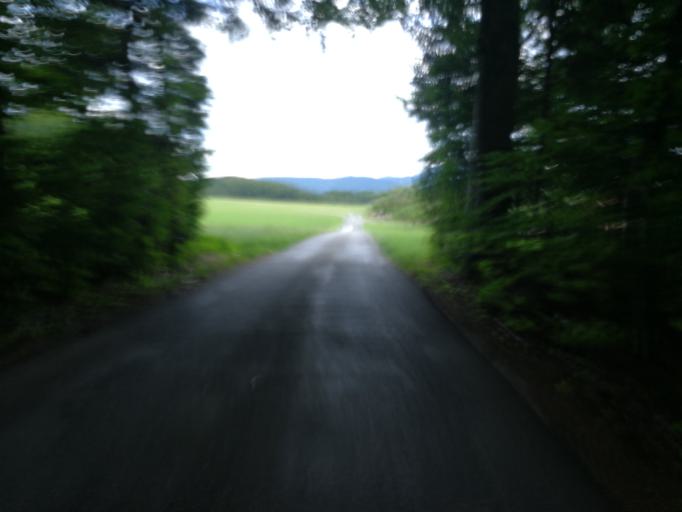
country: AT
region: Salzburg
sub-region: Politischer Bezirk Salzburg-Umgebung
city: Anthering
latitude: 47.8808
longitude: 13.0354
